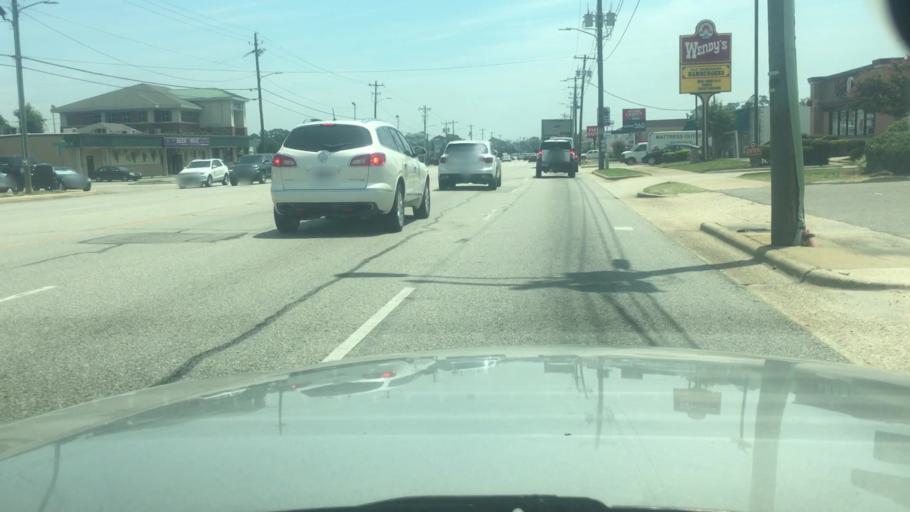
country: US
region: North Carolina
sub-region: Cumberland County
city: Fayetteville
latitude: 35.0450
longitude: -78.9279
